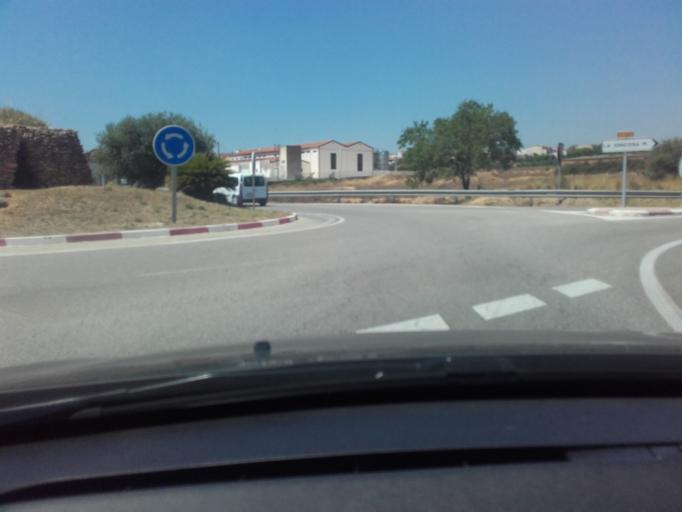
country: ES
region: Catalonia
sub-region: Provincia de Tarragona
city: la Bisbal del Penedes
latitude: 41.2785
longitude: 1.4946
